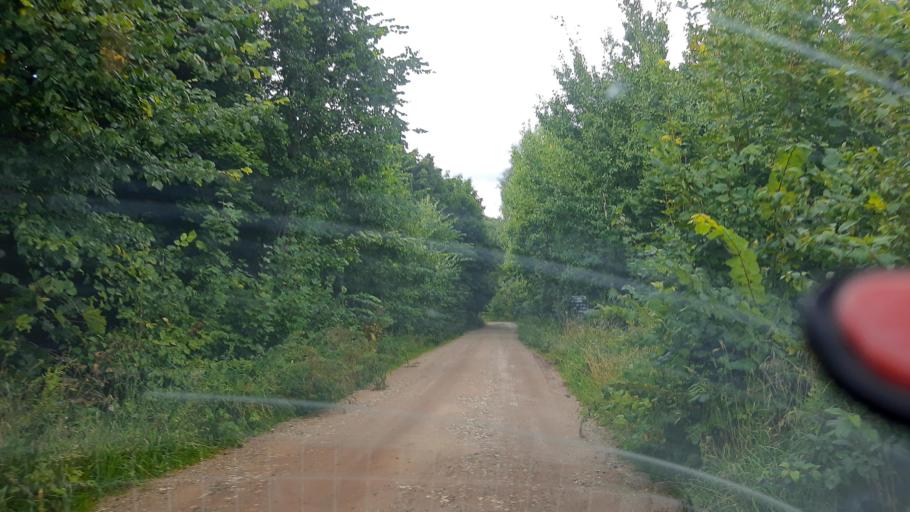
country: RU
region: Bashkortostan
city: Iglino
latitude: 54.7685
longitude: 56.4537
